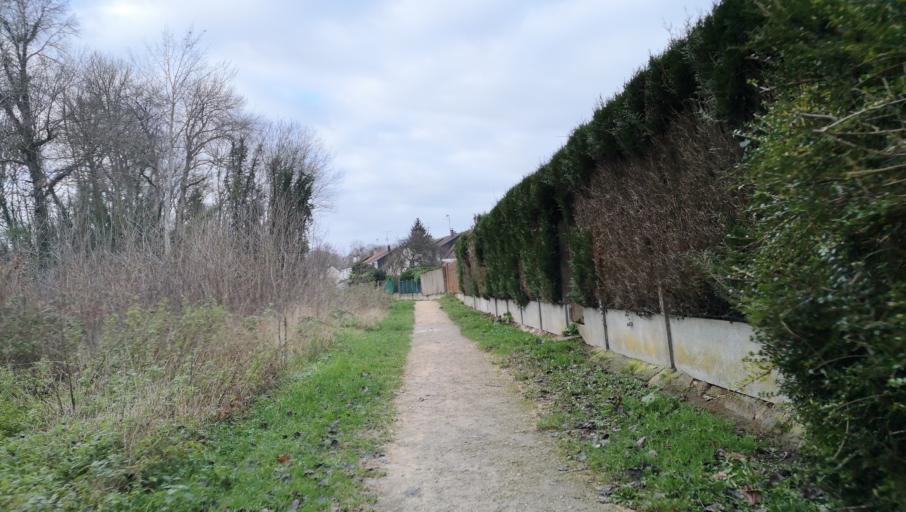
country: FR
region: Centre
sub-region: Departement du Loiret
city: Saint-Jean-de-Braye
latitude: 47.9151
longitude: 1.9982
